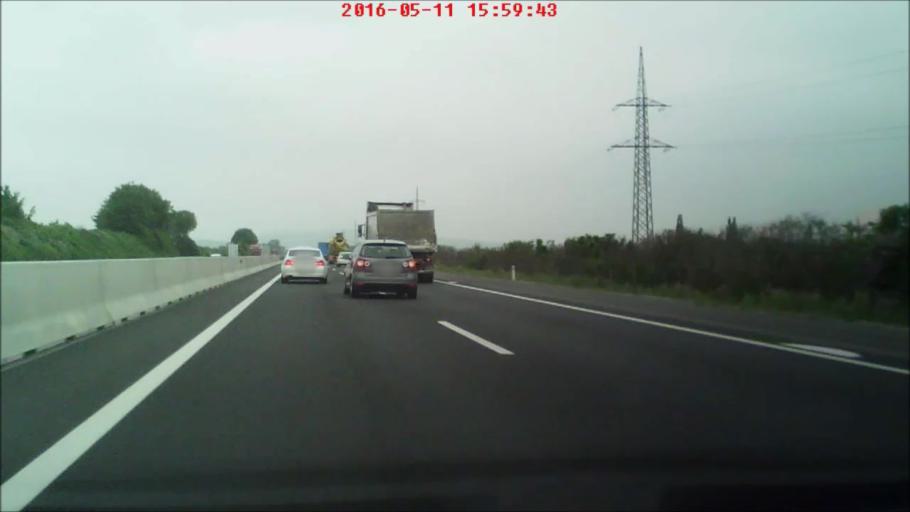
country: AT
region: Styria
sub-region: Politischer Bezirk Graz-Umgebung
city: Zettling
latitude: 46.9586
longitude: 15.4411
